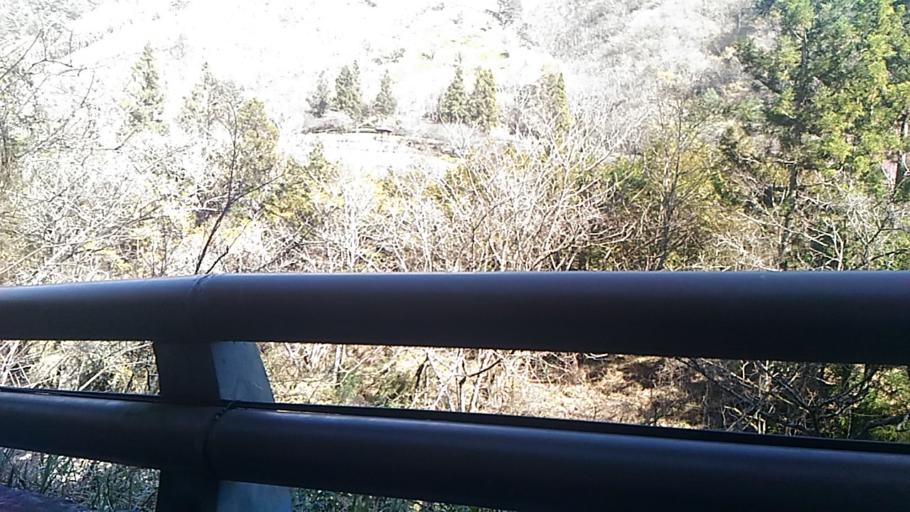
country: TW
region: Taiwan
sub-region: Hualien
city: Hualian
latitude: 24.3590
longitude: 121.3114
